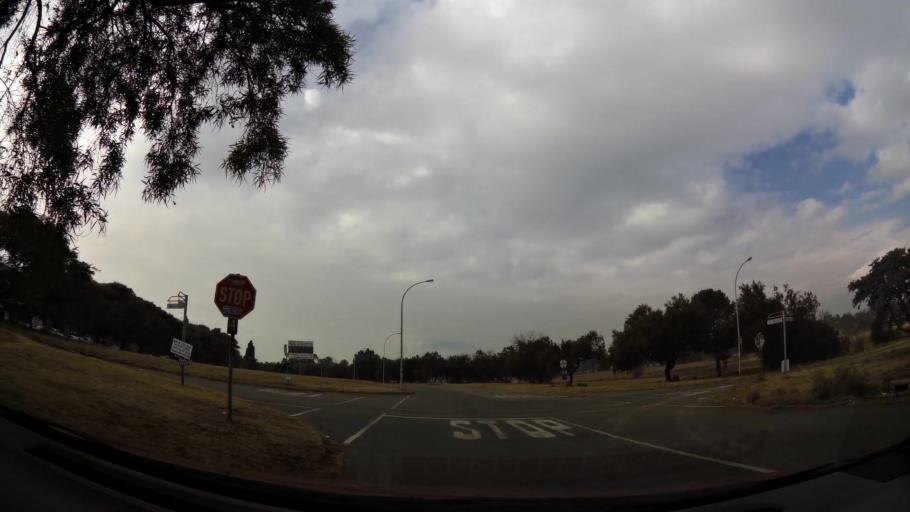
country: ZA
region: Gauteng
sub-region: Sedibeng District Municipality
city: Vanderbijlpark
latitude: -26.7118
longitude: 27.8529
